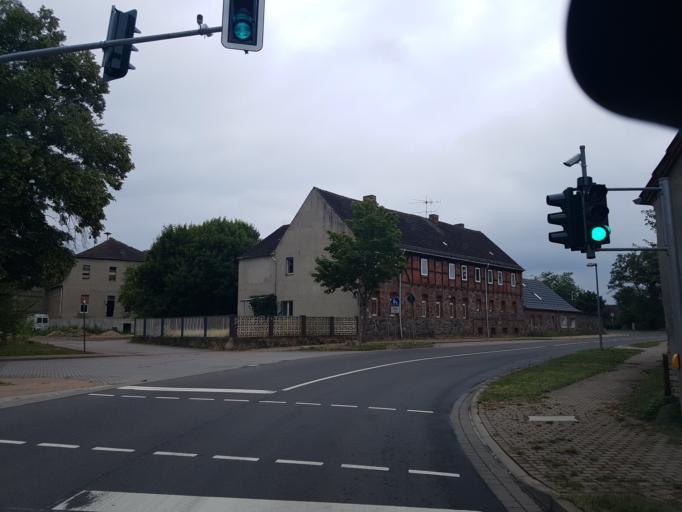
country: DE
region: Saxony-Anhalt
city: Loburg
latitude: 52.2413
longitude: 12.0485
